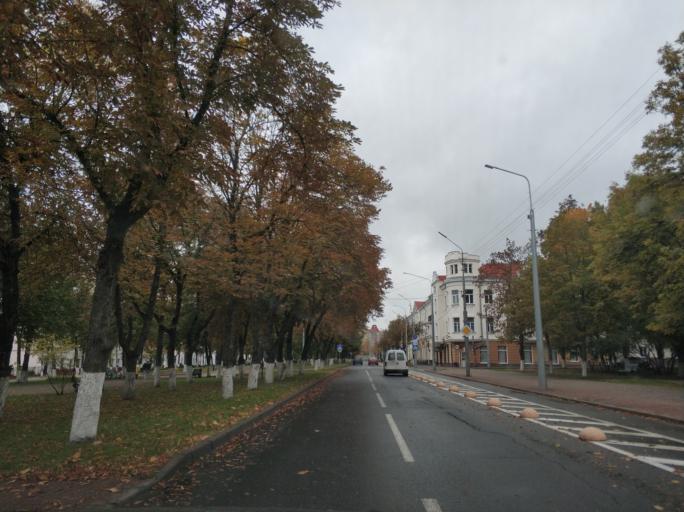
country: BY
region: Vitebsk
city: Polatsk
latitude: 55.4851
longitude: 28.7735
